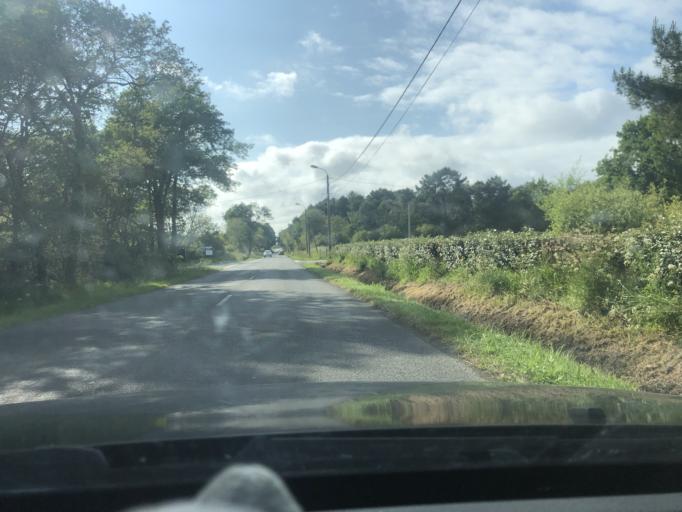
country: FR
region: Brittany
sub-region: Departement du Morbihan
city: Sainte-Helene
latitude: 47.6912
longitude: -3.2340
